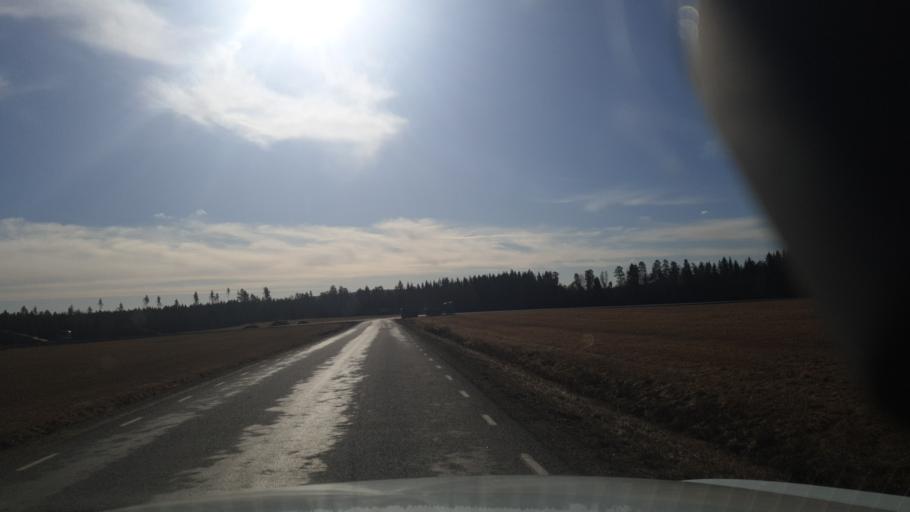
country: SE
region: Vaermland
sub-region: Eda Kommun
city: Charlottenberg
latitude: 59.7798
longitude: 12.1666
